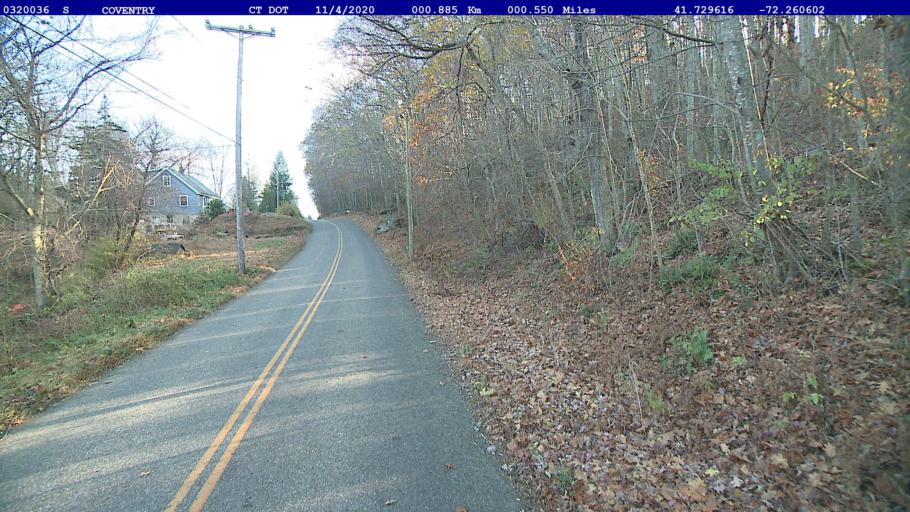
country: US
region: Connecticut
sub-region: Tolland County
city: Mansfield City
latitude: 41.7296
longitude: -72.2606
